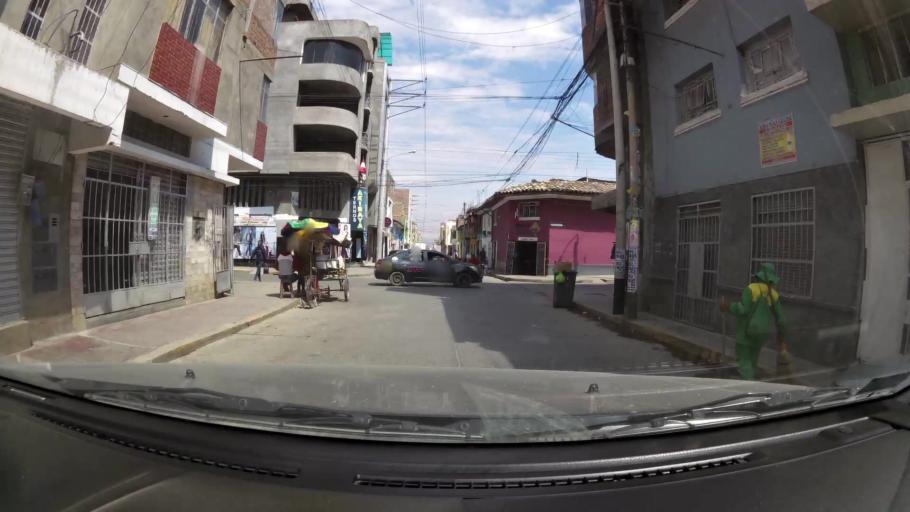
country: PE
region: Junin
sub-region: Provincia de Huancayo
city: El Tambo
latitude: -12.0719
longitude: -75.2125
